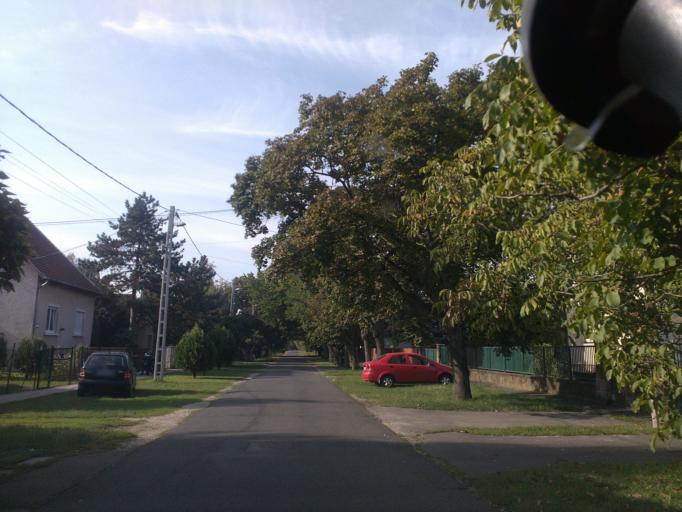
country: HU
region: Pest
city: Gyal
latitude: 47.4249
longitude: 19.2161
